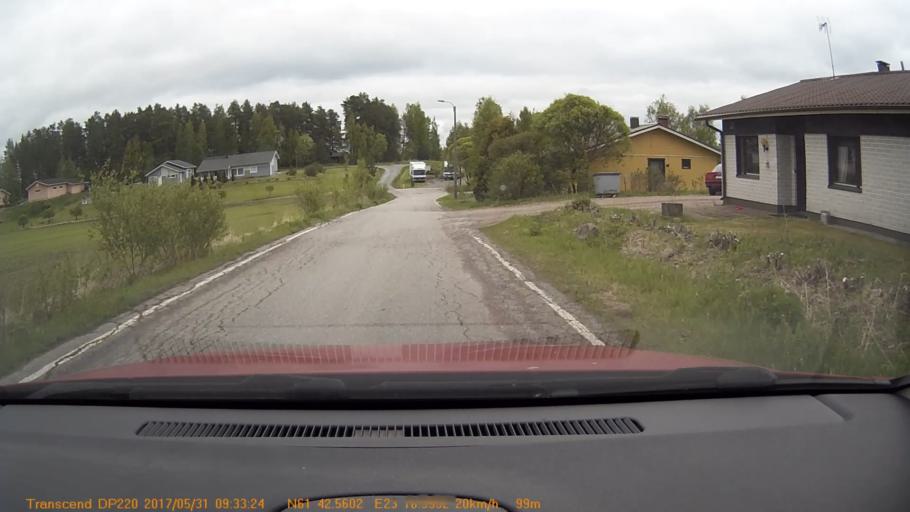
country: FI
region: Pirkanmaa
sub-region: Tampere
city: Viljakkala
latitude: 61.7094
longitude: 23.2836
